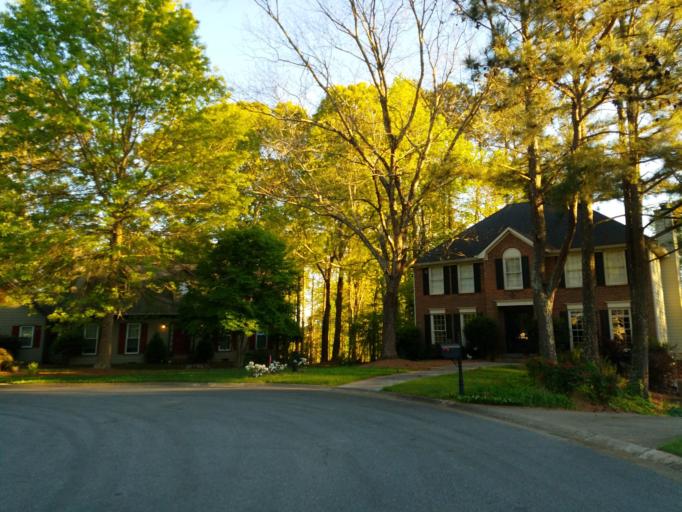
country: US
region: Georgia
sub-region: Cobb County
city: Powder Springs
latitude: 33.9210
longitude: -84.6362
